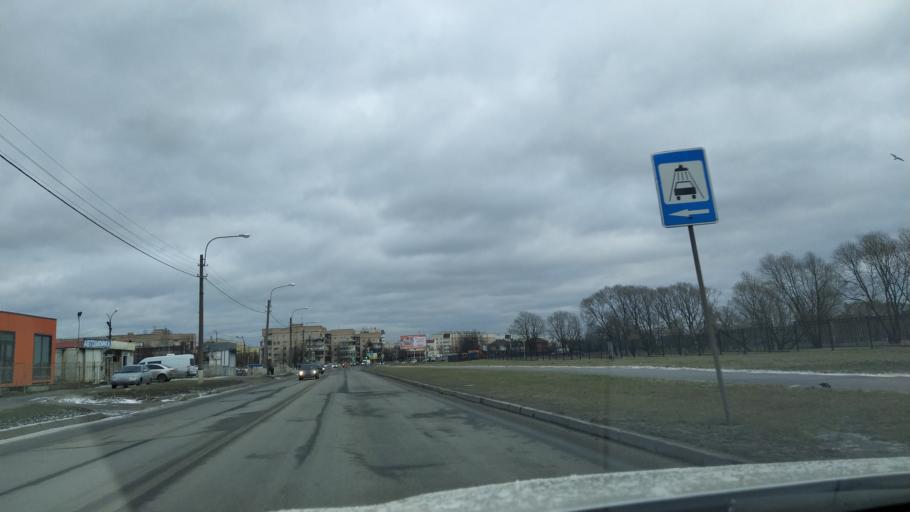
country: RU
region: St.-Petersburg
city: Pushkin
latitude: 59.7337
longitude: 30.3897
